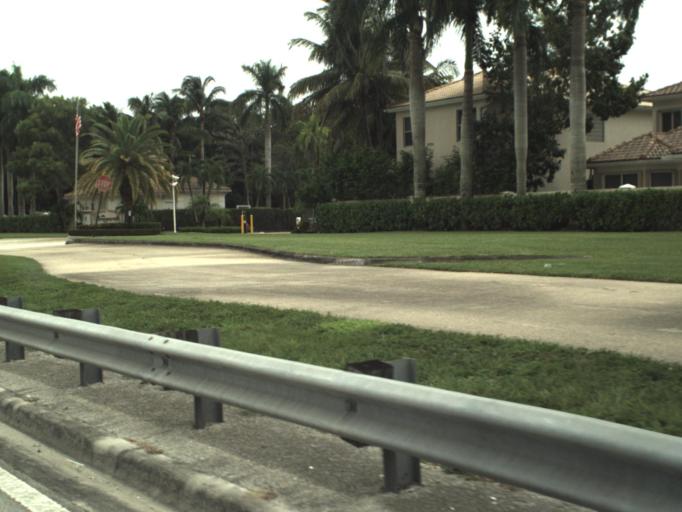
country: US
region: Florida
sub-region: Palm Beach County
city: Boca Pointe
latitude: 26.3493
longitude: -80.1980
